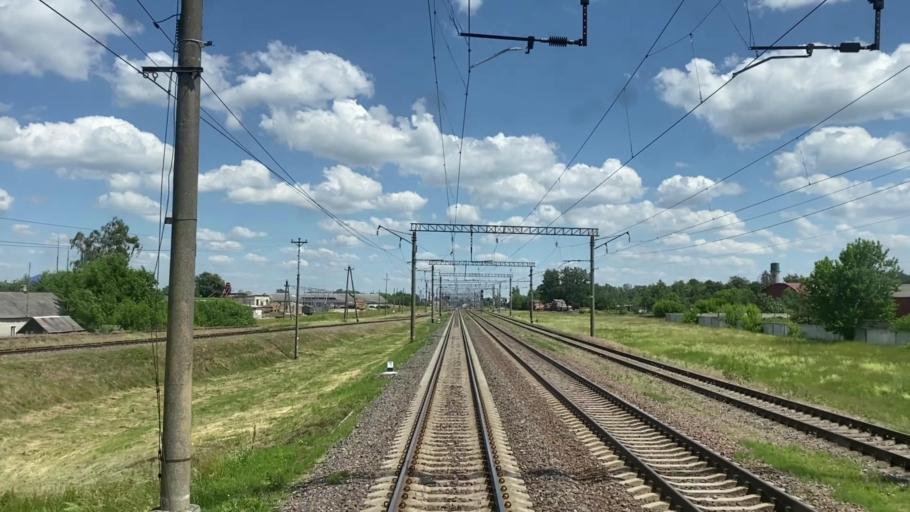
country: BY
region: Brest
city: Ivatsevichy
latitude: 52.7009
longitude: 25.3263
